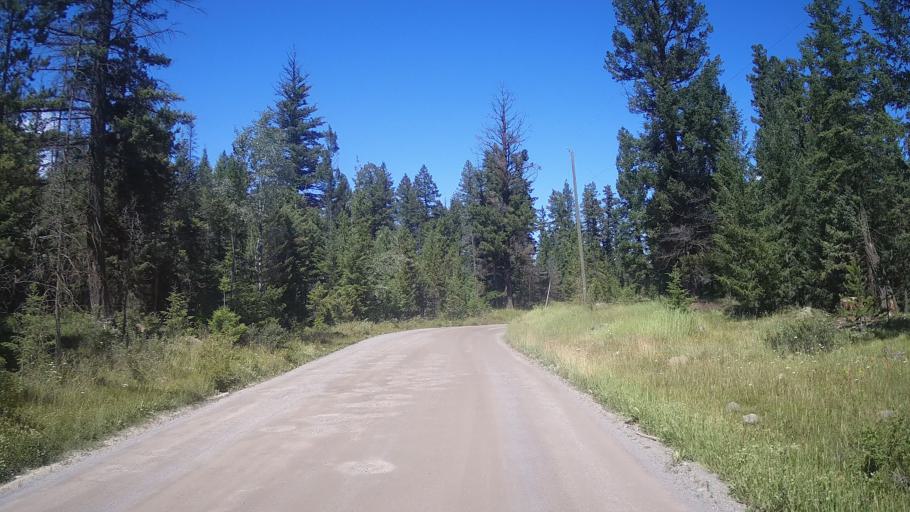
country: CA
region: British Columbia
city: Cache Creek
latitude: 51.1953
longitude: -121.5902
